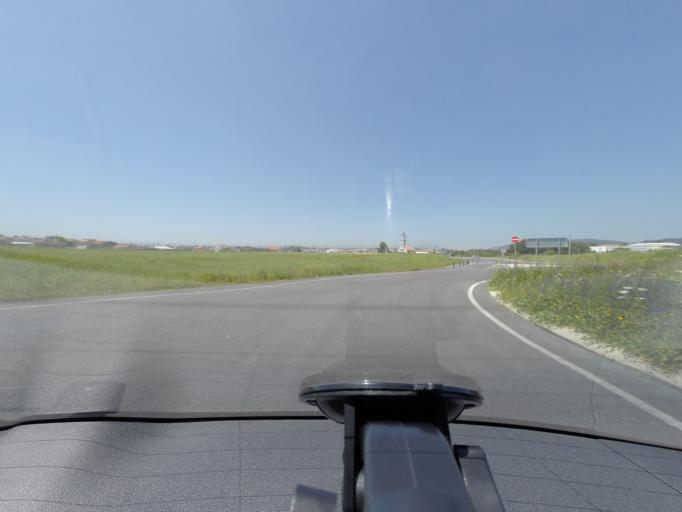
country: PT
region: Lisbon
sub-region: Cascais
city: Parede
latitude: 38.7326
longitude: -9.3566
